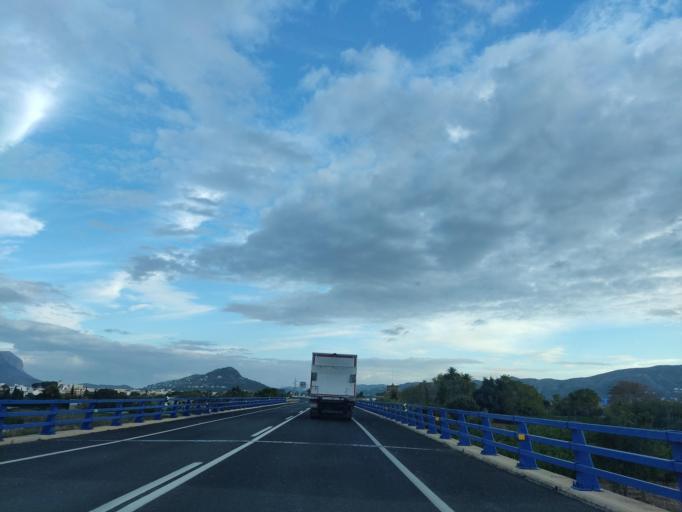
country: ES
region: Valencia
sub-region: Provincia de Alicante
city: Beniarbeig
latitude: 38.8282
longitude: 0.0065
